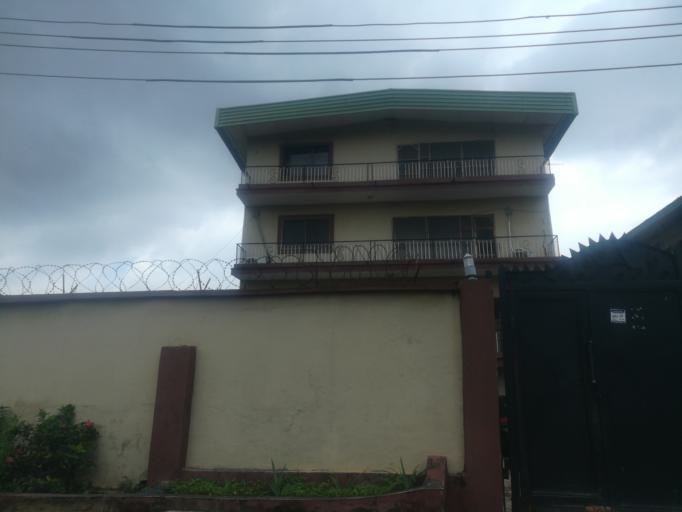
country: NG
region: Lagos
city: Somolu
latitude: 6.5573
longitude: 3.3944
